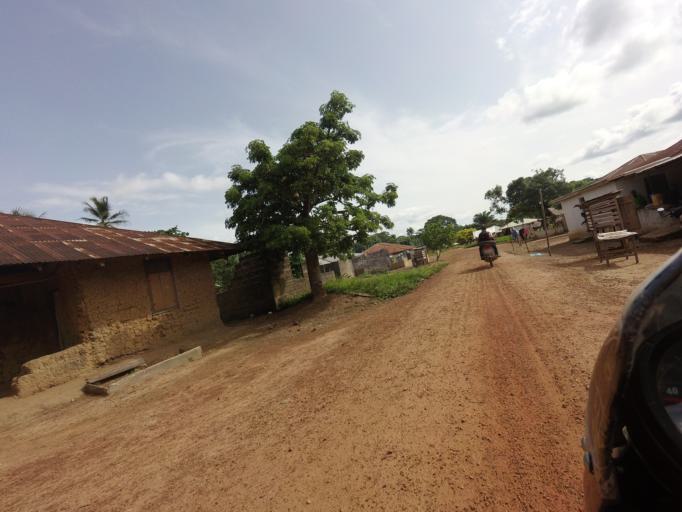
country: SL
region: Eastern Province
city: Jojoima
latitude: 7.8507
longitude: -10.8060
